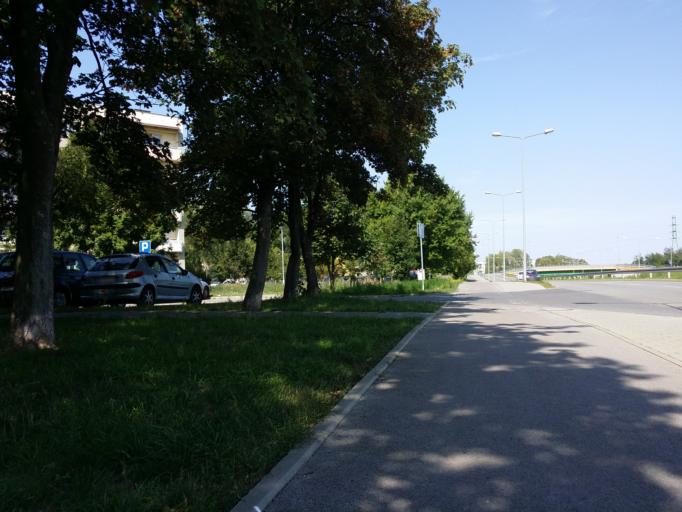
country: PL
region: Masovian Voivodeship
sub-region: Radom
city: Radom
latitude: 51.3742
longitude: 21.1648
